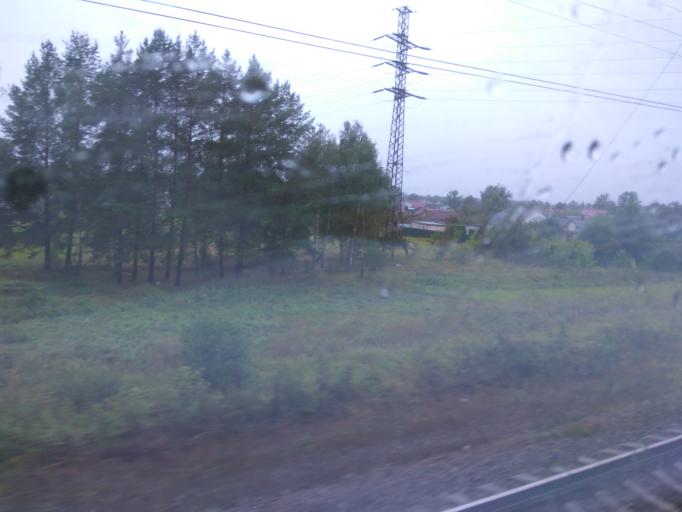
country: RU
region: Moskovskaya
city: Zhilevo
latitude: 54.9786
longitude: 38.0349
